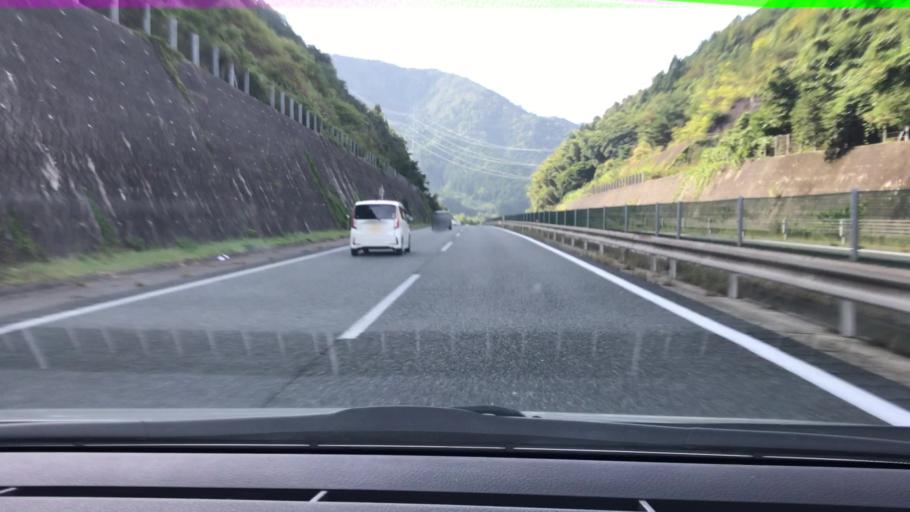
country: JP
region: Hyogo
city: Sasayama
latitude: 35.0421
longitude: 135.1825
